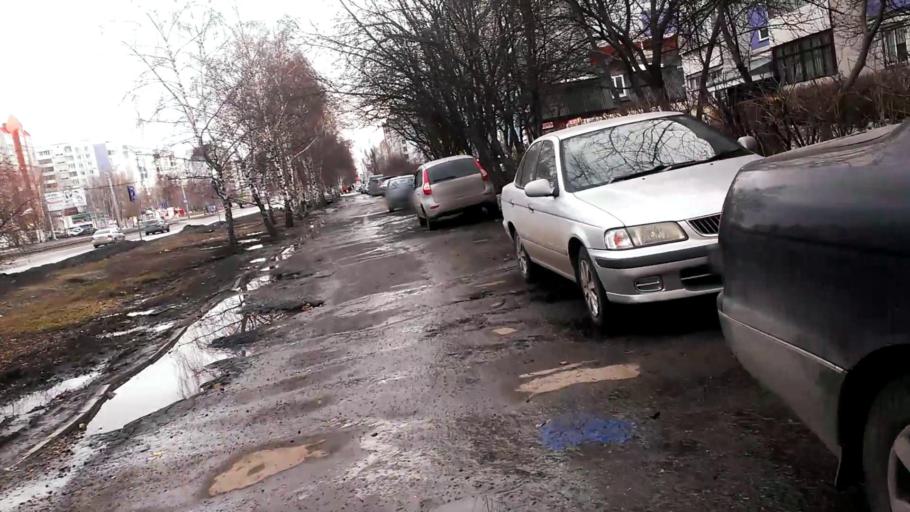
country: RU
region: Altai Krai
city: Novoaltaysk
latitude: 53.3754
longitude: 83.9213
